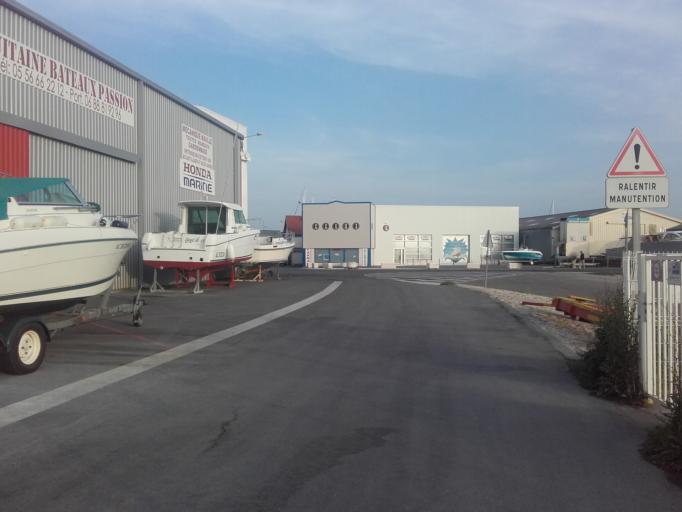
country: FR
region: Aquitaine
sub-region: Departement de la Gironde
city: Gujan-Mestras
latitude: 44.6423
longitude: -1.0716
